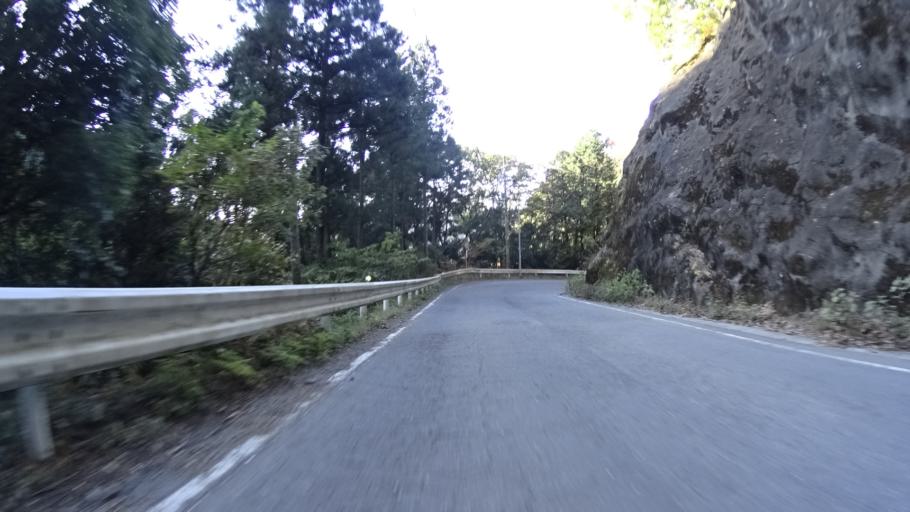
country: JP
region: Yamanashi
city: Uenohara
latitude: 35.6796
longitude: 139.0982
